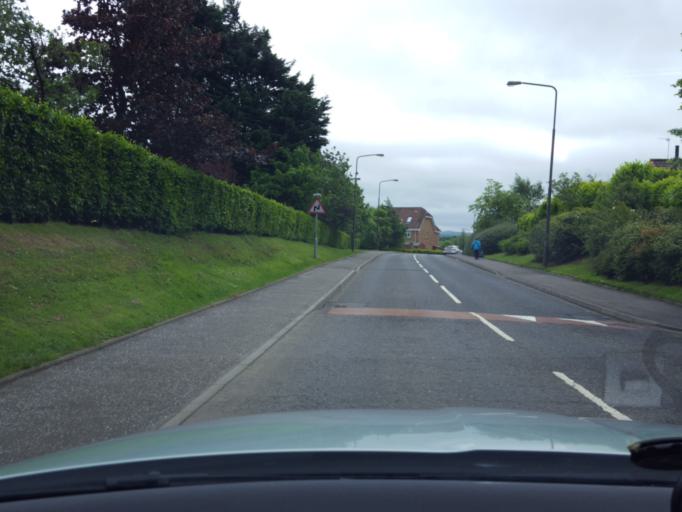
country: GB
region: Scotland
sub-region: West Lothian
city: Broxburn
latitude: 55.9303
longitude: -3.4968
